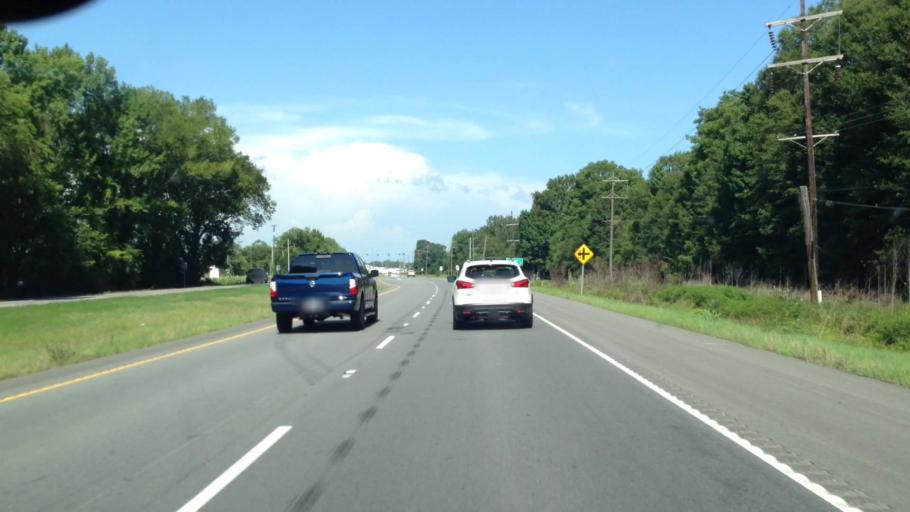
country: US
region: Louisiana
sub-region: Saint Landry Parish
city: Port Barre
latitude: 30.5474
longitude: -91.9453
